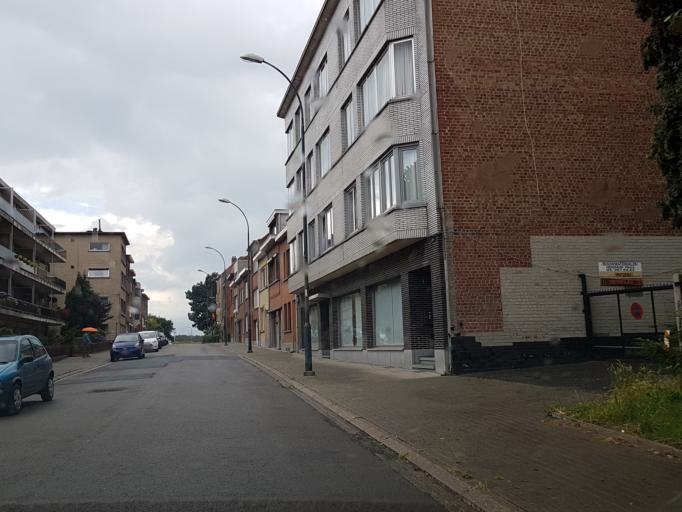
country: BE
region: Flanders
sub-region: Provincie Vlaams-Brabant
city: Bever
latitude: 50.9126
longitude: 4.3480
